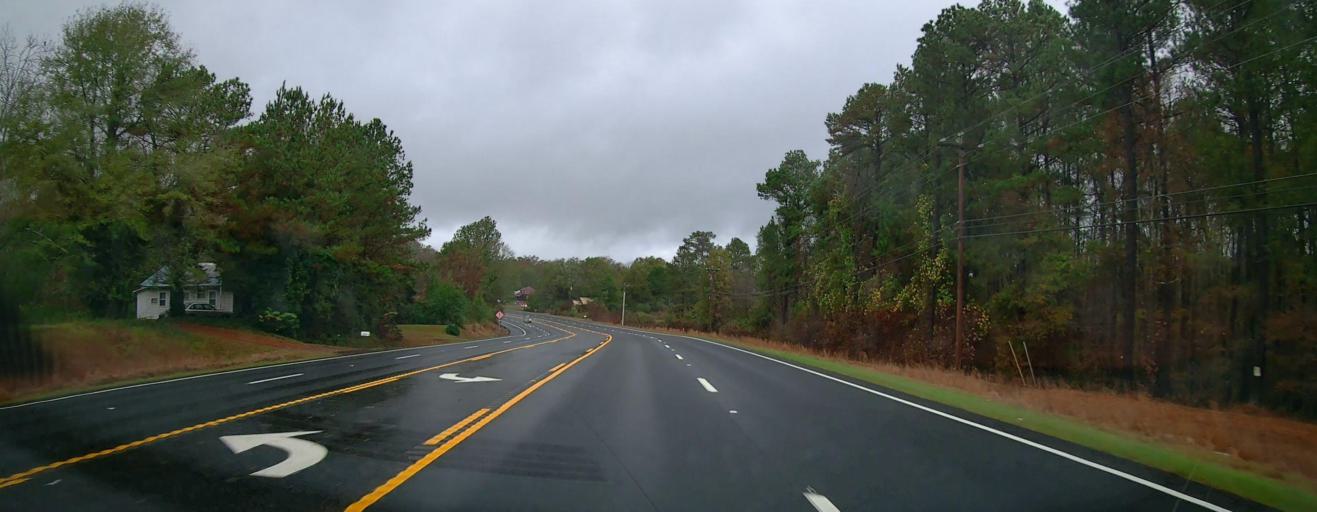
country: US
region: Georgia
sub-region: Clarke County
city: Country Club Estates
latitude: 34.0122
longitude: -83.3873
